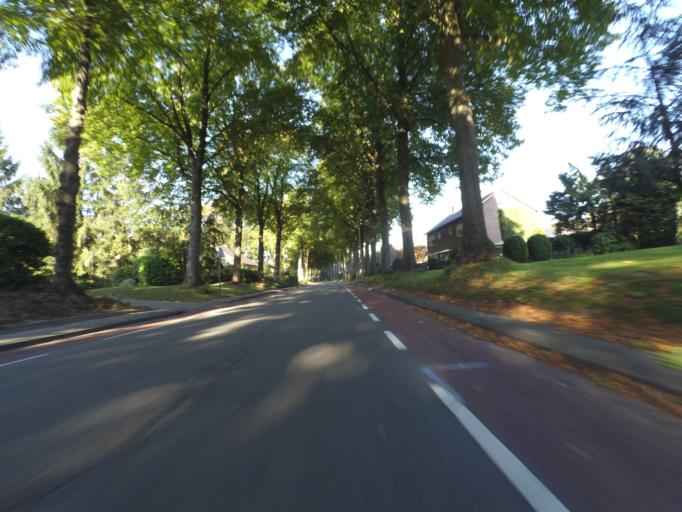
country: NL
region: Gelderland
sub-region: Gemeente Putten
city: Putten
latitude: 52.2632
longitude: 5.5867
